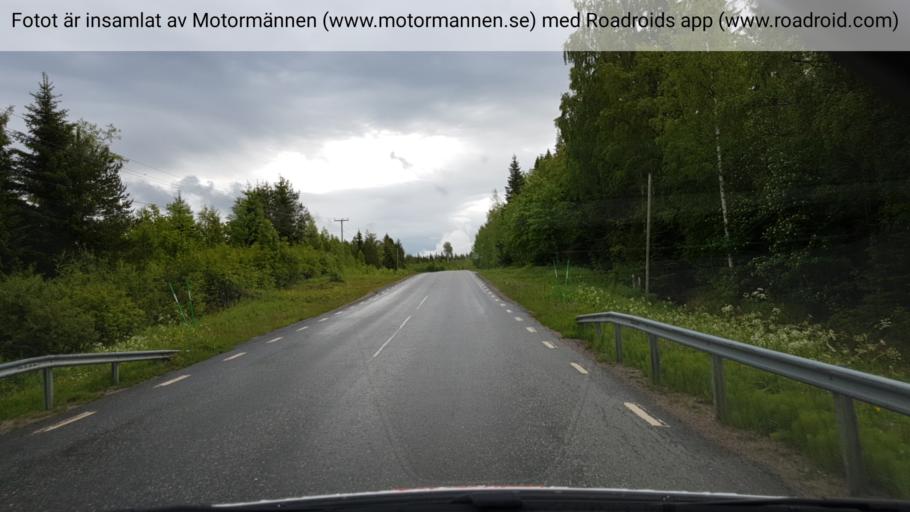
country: SE
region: Vaesterbotten
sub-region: Vannas Kommun
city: Vannasby
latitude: 63.8510
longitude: 19.9420
